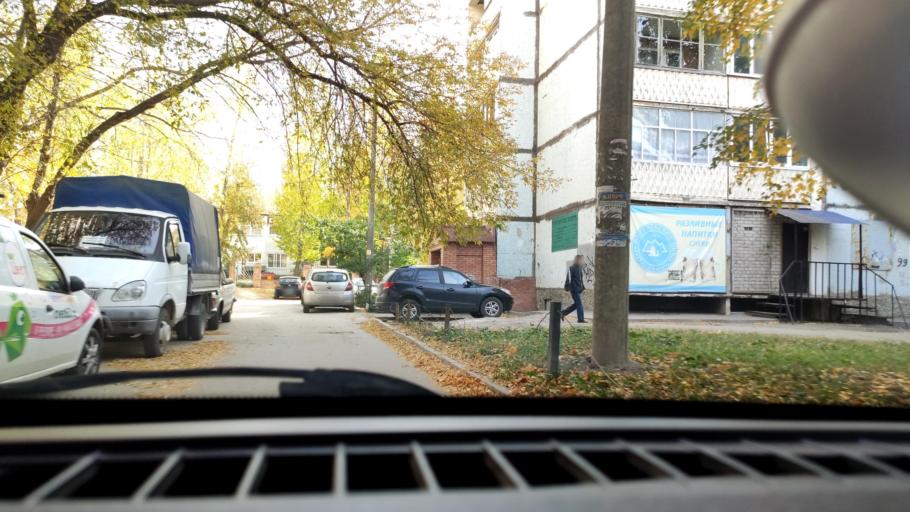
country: RU
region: Samara
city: Samara
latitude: 53.2603
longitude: 50.2269
